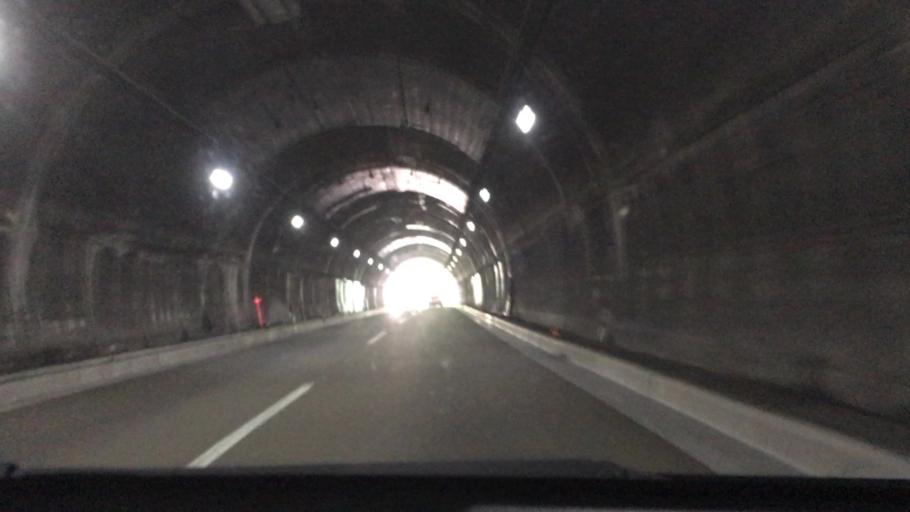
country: JP
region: Yamaguchi
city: Shimonoseki
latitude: 33.9535
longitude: 130.9816
